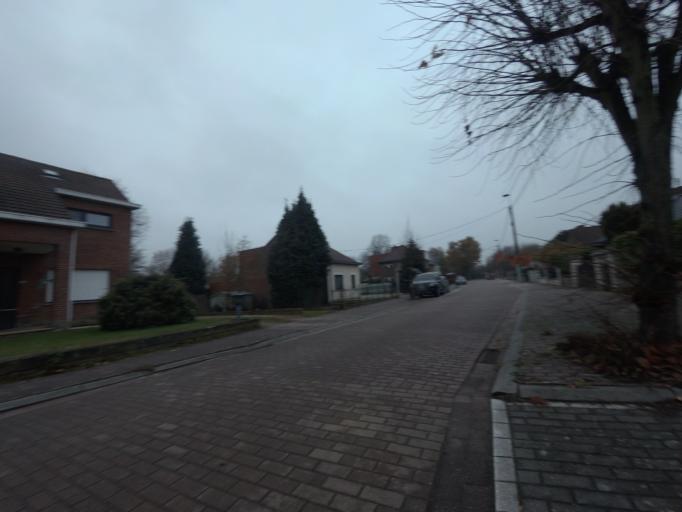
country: BE
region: Flanders
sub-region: Provincie Vlaams-Brabant
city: Kortenberg
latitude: 50.8842
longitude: 4.5236
